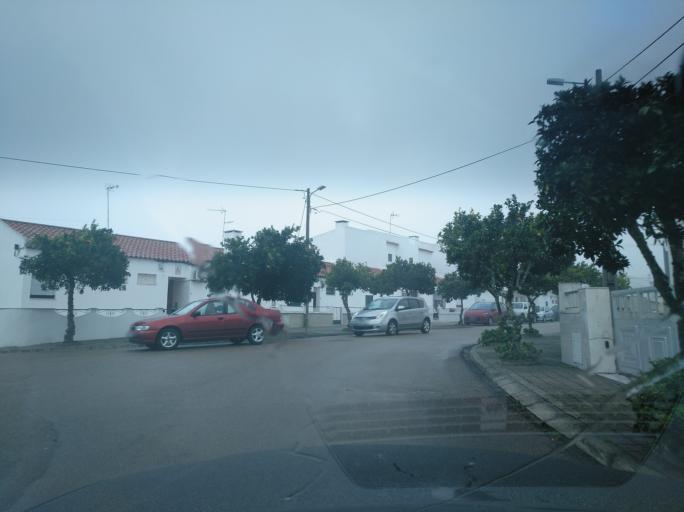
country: PT
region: Portalegre
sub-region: Campo Maior
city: Campo Maior
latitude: 39.0185
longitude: -7.0667
